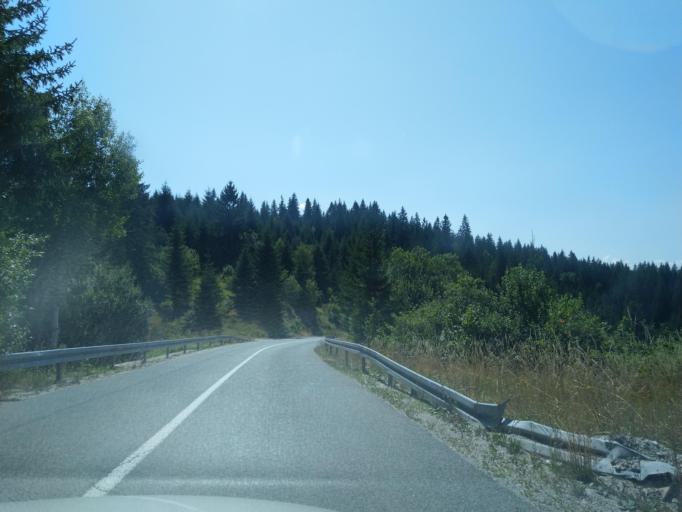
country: RS
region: Central Serbia
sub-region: Zlatiborski Okrug
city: Nova Varos
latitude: 43.4026
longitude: 19.8441
